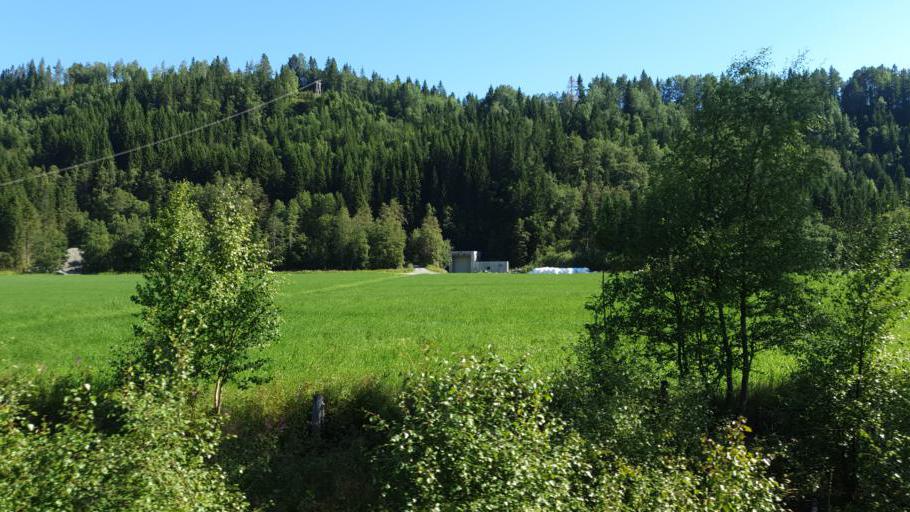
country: NO
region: Sor-Trondelag
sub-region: Meldal
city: Meldal
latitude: 63.1792
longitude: 9.7618
